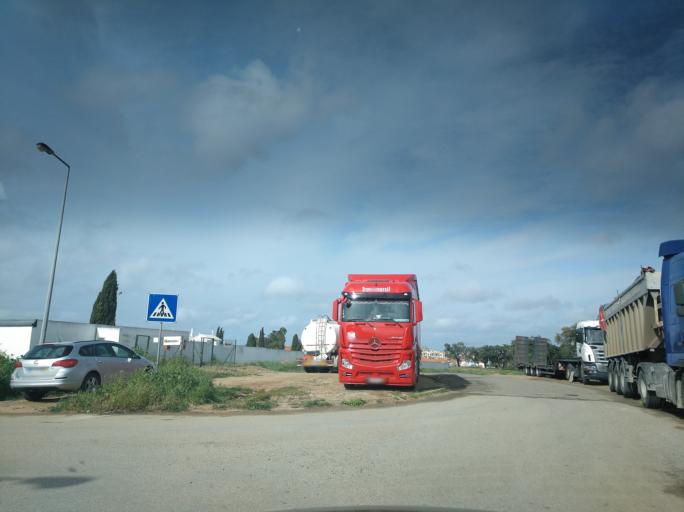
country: PT
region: Setubal
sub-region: Grandola
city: Grandola
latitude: 38.1726
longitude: -8.5591
